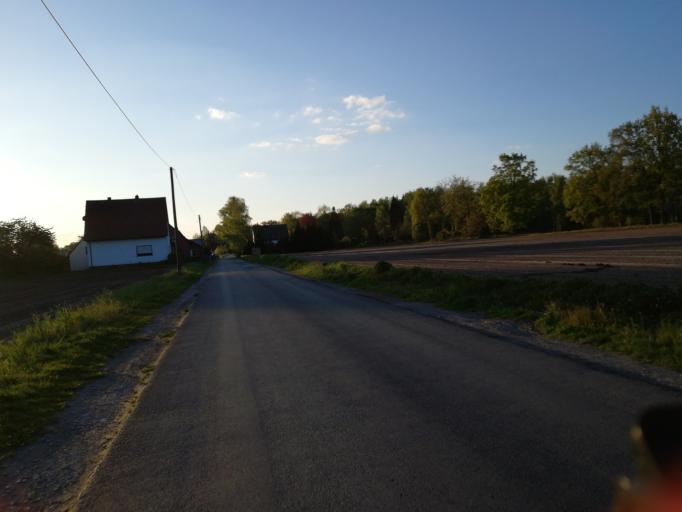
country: DE
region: North Rhine-Westphalia
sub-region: Regierungsbezirk Detmold
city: Verl
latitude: 51.9300
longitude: 8.4771
